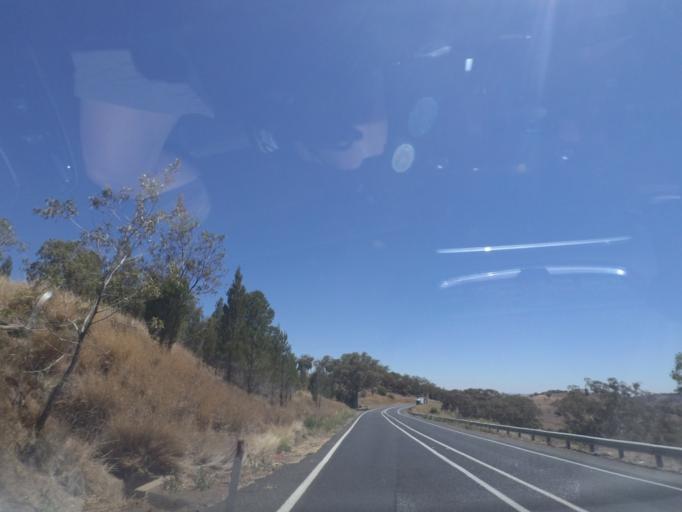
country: AU
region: New South Wales
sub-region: Warrumbungle Shire
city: Coonabarabran
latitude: -31.4532
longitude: 149.0162
